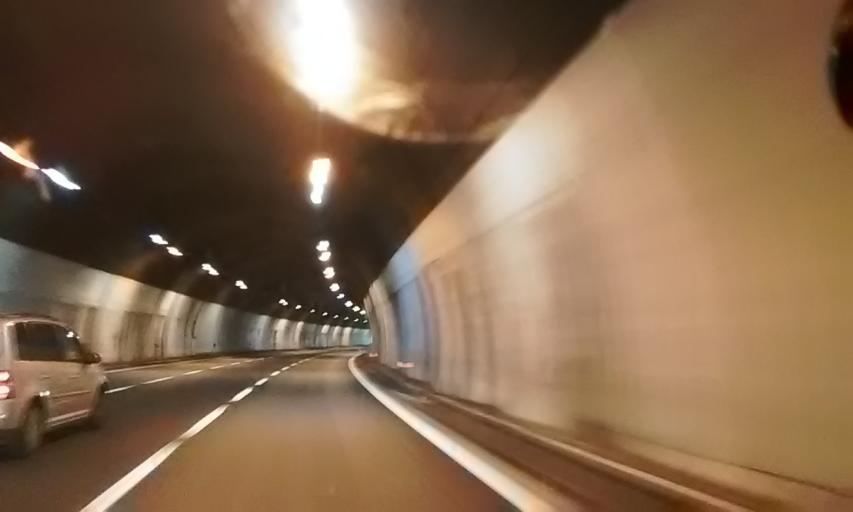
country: IT
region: Liguria
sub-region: Provincia di Genova
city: Rossiglione
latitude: 44.5644
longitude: 8.6637
